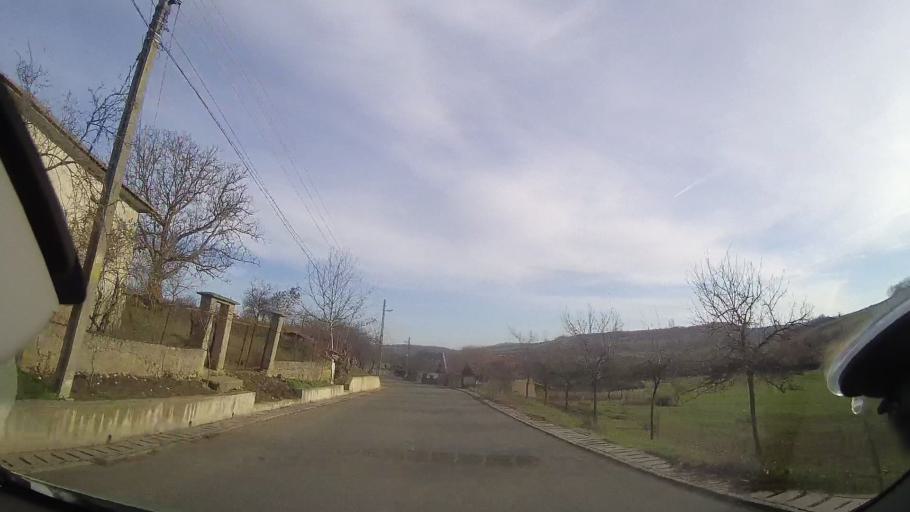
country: RO
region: Bihor
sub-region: Comuna Sarbi
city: Burzuc
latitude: 47.1481
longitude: 22.1774
